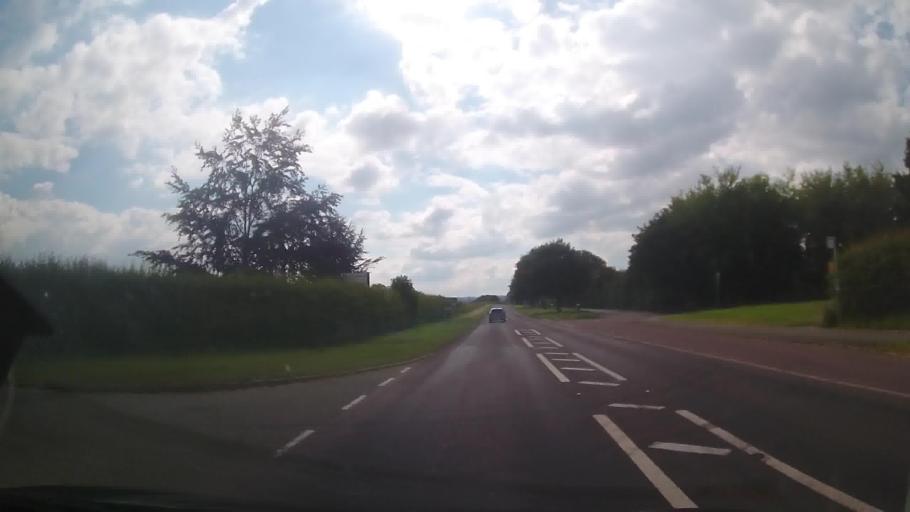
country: GB
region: England
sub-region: Shropshire
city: Whittington
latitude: 52.8715
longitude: -3.0157
